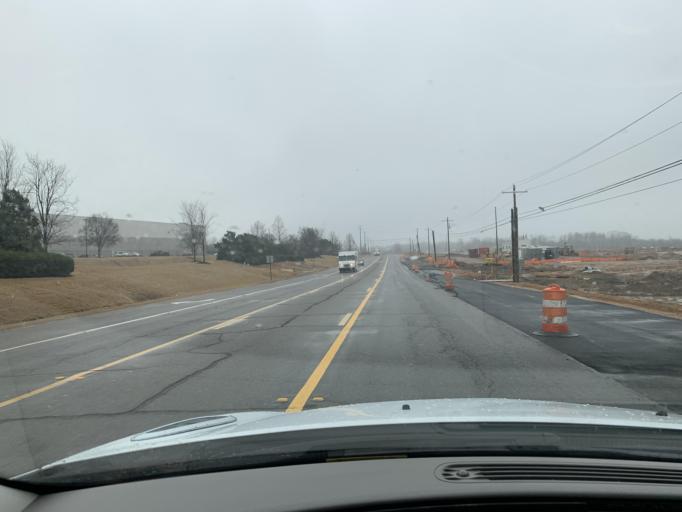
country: US
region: Mississippi
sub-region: De Soto County
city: Horn Lake
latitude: 34.9182
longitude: -90.0060
